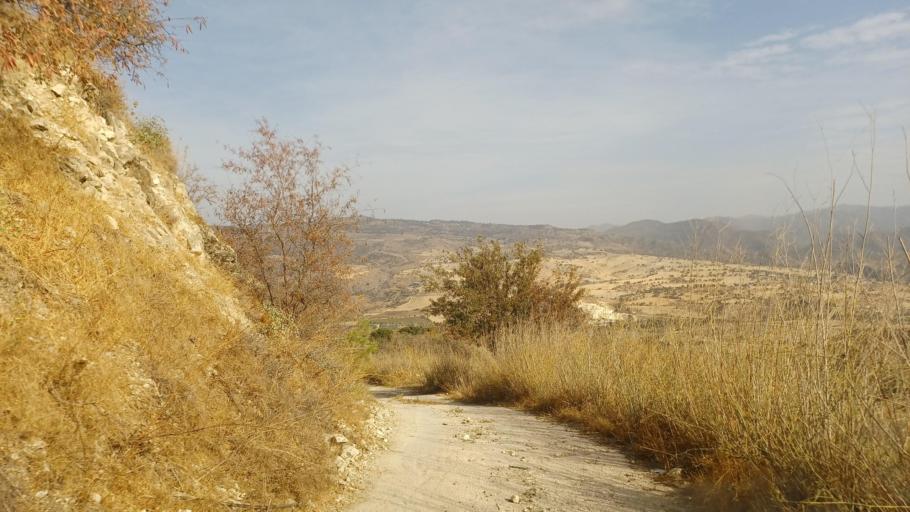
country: CY
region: Pafos
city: Polis
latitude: 34.9419
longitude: 32.5156
